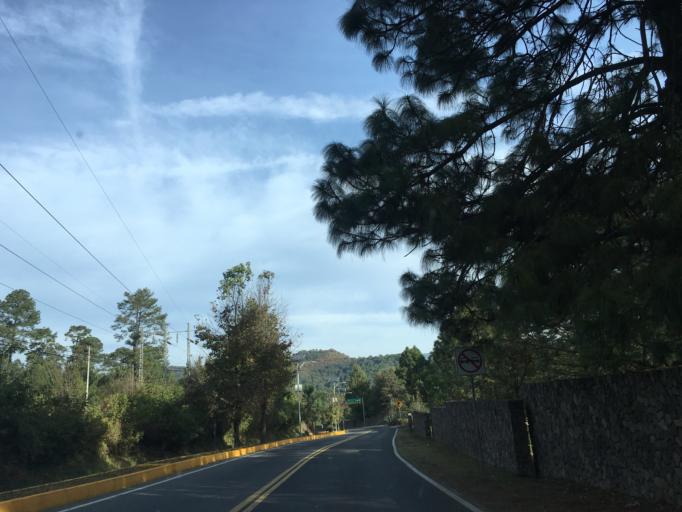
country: MX
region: Mexico
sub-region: Valle de Bravo
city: Colonia Rincon Villa del Valle
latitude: 19.1996
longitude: -100.0999
